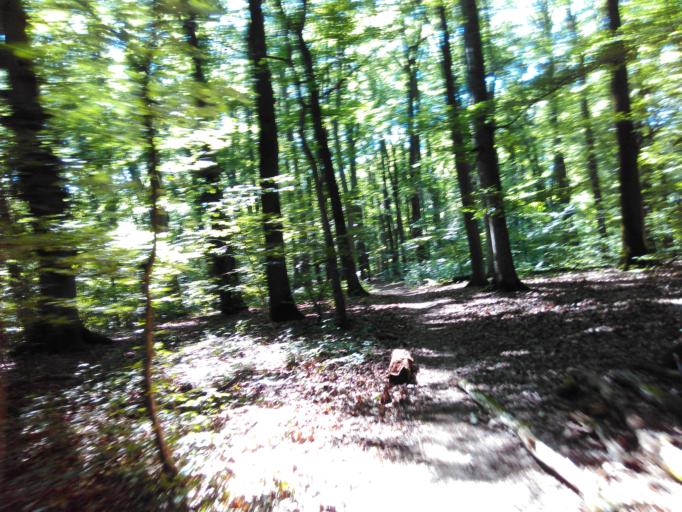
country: LU
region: Luxembourg
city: Pontpierre
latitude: 49.5588
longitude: 6.0338
